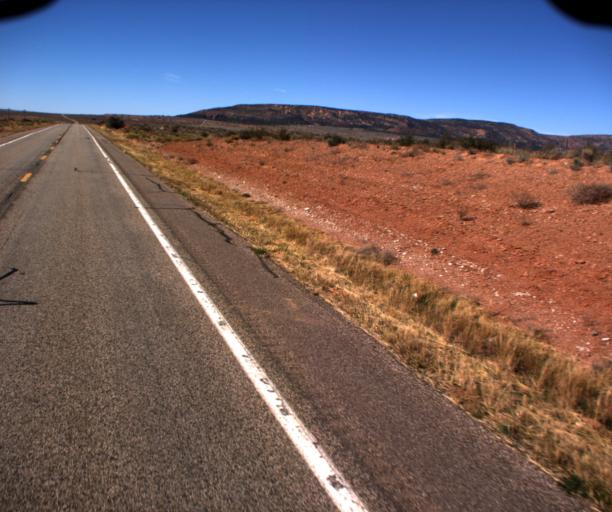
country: US
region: Arizona
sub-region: Coconino County
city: Fredonia
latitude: 36.8721
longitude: -112.6758
